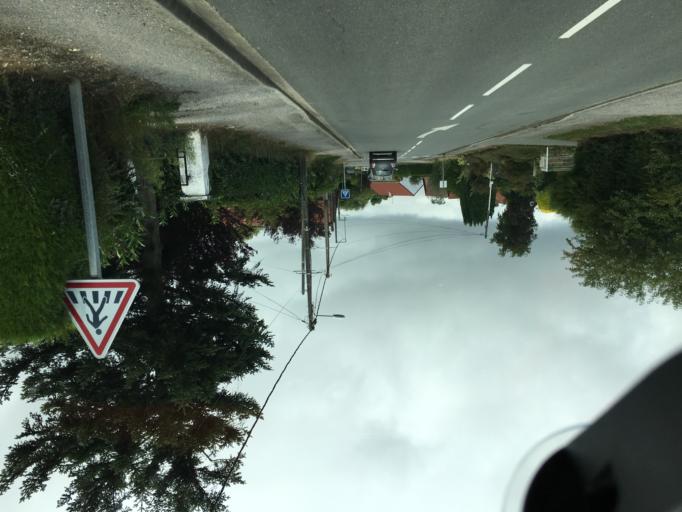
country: FR
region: Nord-Pas-de-Calais
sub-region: Departement du Pas-de-Calais
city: Montreuil
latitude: 50.4355
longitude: 1.7169
